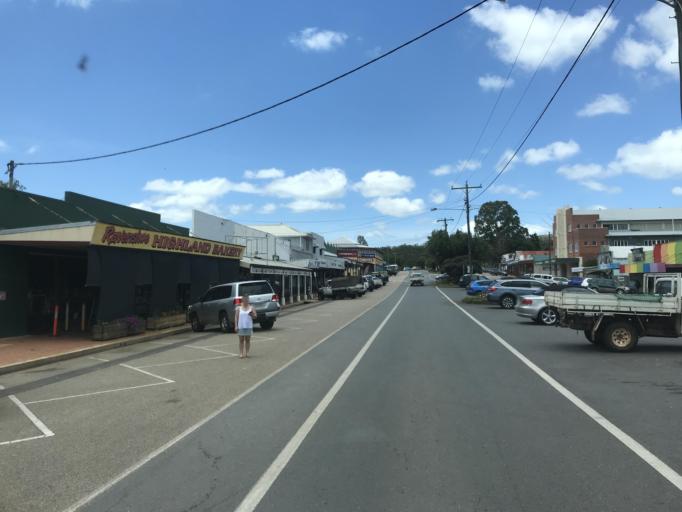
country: AU
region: Queensland
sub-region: Tablelands
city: Ravenshoe
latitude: -17.6074
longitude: 145.4829
